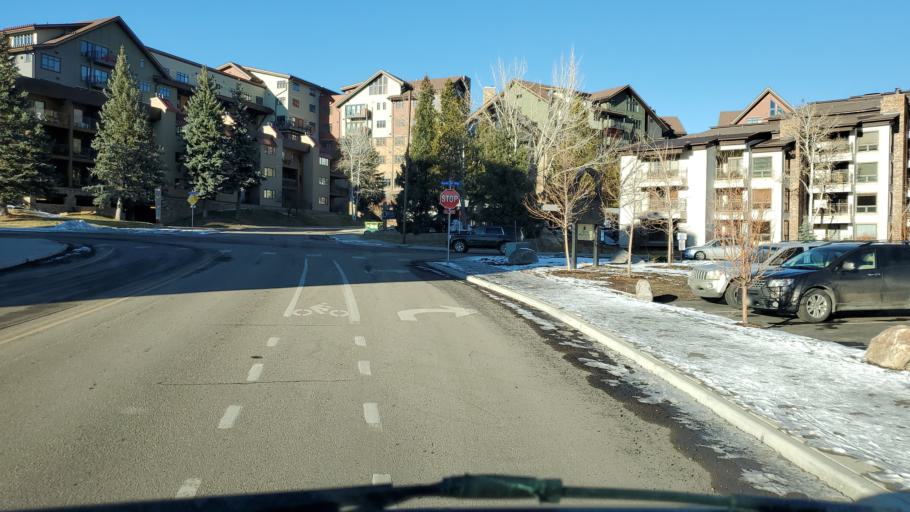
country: US
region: Colorado
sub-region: Routt County
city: Steamboat Springs
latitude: 40.4551
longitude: -106.8053
